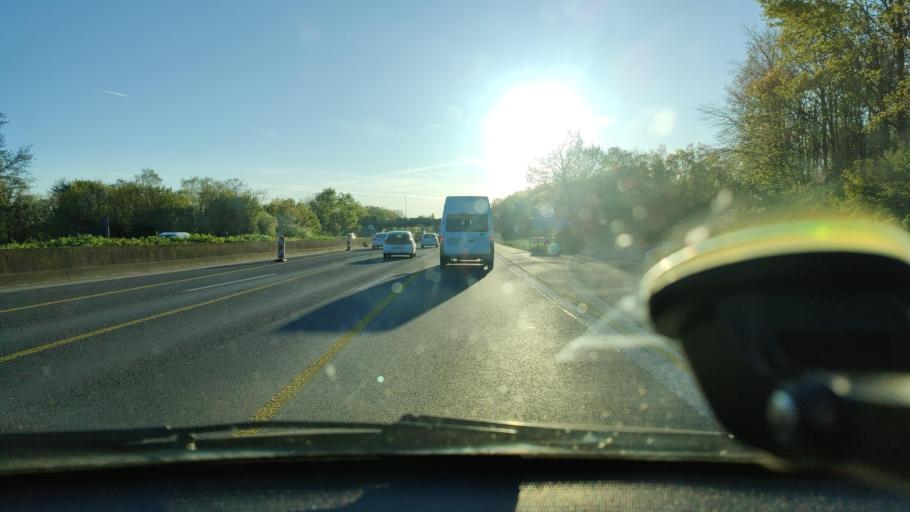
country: DE
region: North Rhine-Westphalia
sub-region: Regierungsbezirk Munster
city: Bottrop
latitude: 51.5396
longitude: 6.8738
